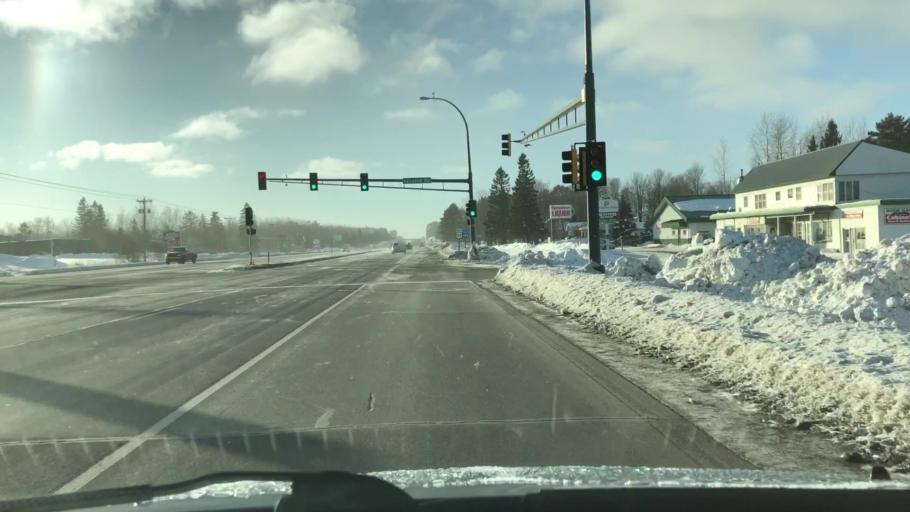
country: US
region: Minnesota
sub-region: Saint Louis County
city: Hermantown
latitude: 46.8368
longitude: -92.2165
